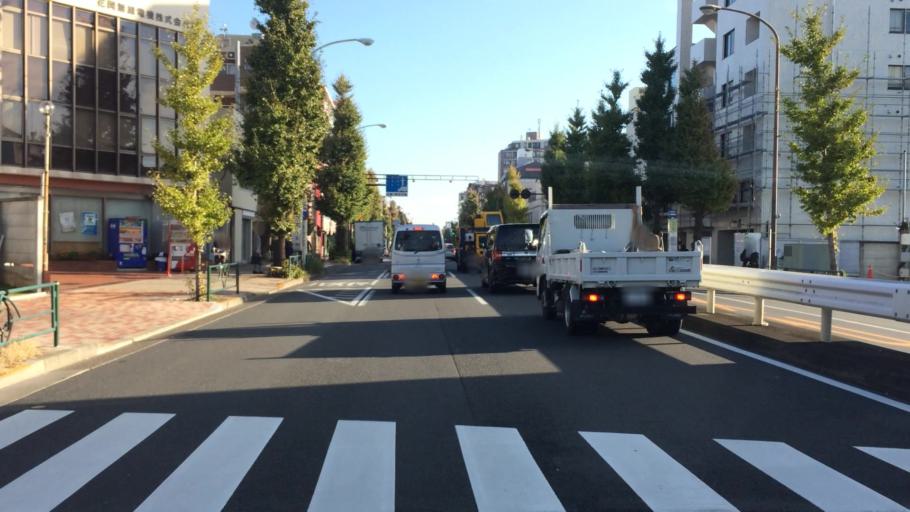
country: JP
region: Tokyo
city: Tokyo
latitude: 35.6242
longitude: 139.6868
